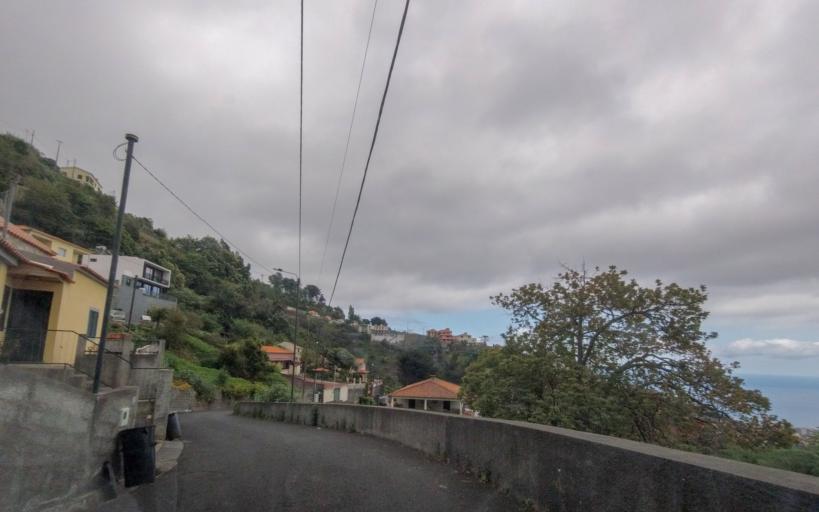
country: PT
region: Madeira
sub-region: Funchal
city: Nossa Senhora do Monte
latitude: 32.6769
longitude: -16.9137
